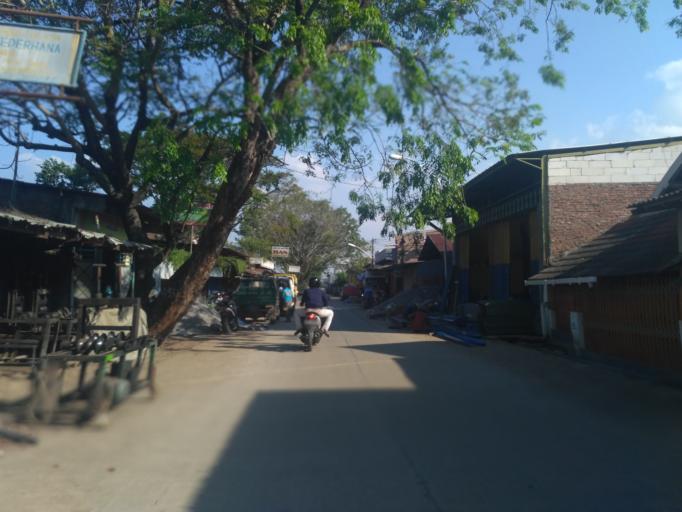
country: ID
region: Central Java
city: Semarang
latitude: -6.9665
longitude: 110.4431
